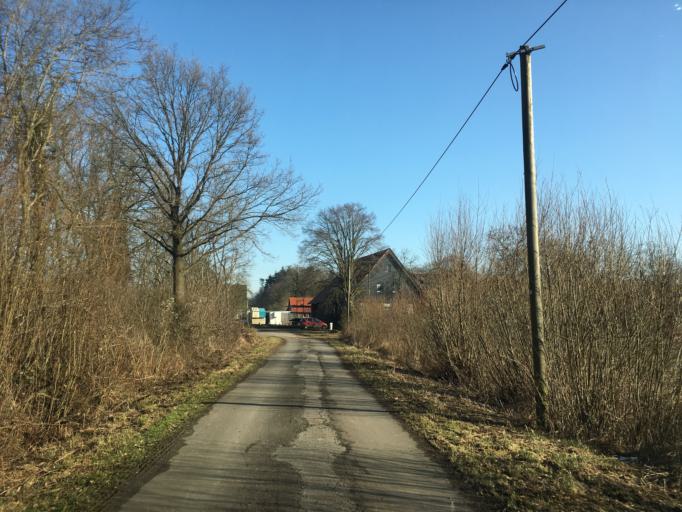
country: DE
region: North Rhine-Westphalia
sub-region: Regierungsbezirk Munster
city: Altenberge
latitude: 52.0090
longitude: 7.5150
